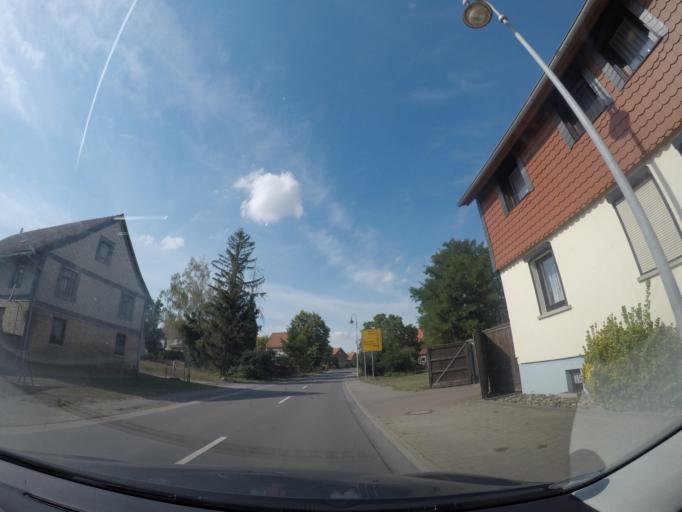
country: DE
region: Saxony-Anhalt
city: Langeln
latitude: 51.9145
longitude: 10.7927
